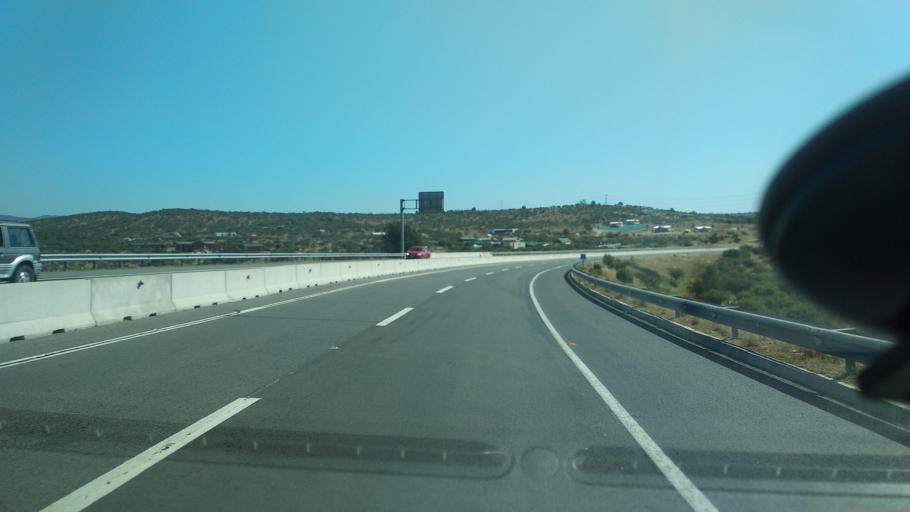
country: CL
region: Valparaiso
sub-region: Provincia de Marga Marga
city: Limache
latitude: -32.9846
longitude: -71.3184
